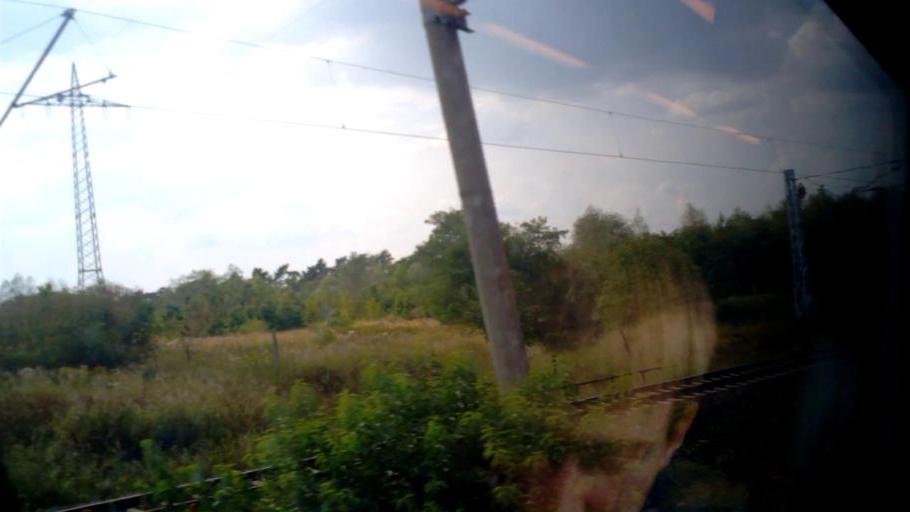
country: DE
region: Brandenburg
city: Ludwigsfelde
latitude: 52.3332
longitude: 13.2577
